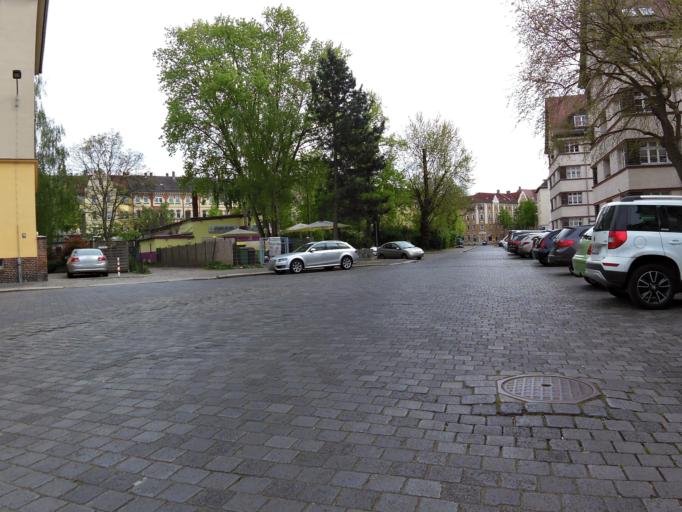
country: DE
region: Saxony
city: Leipzig
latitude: 51.3549
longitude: 12.4113
